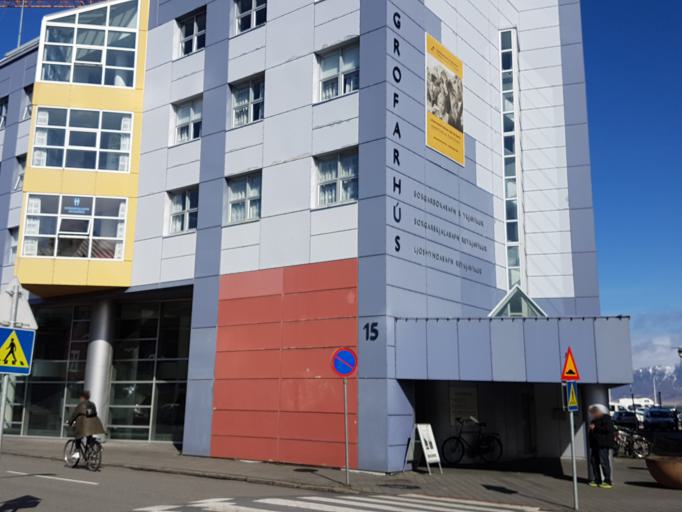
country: IS
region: Capital Region
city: Kopavogur
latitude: 64.1493
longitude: -21.9416
